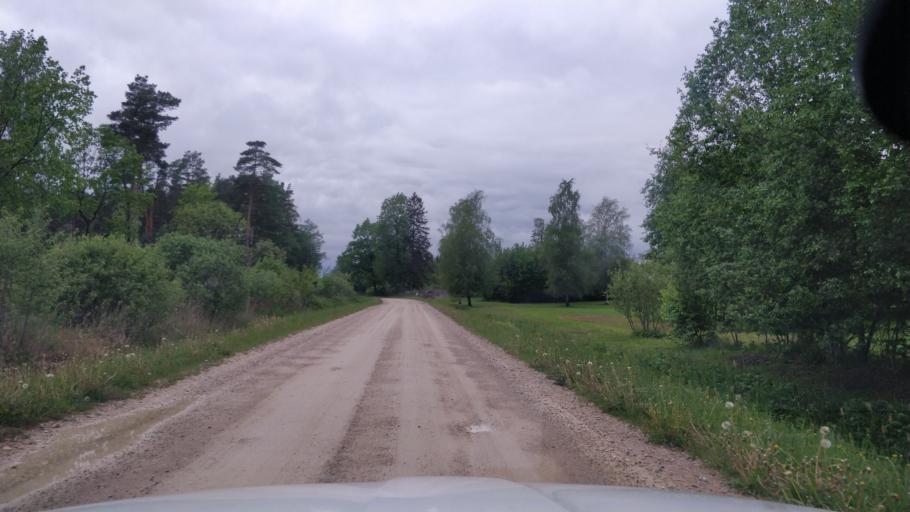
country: EE
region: Paernumaa
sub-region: Halinga vald
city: Parnu-Jaagupi
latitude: 58.7098
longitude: 24.3499
